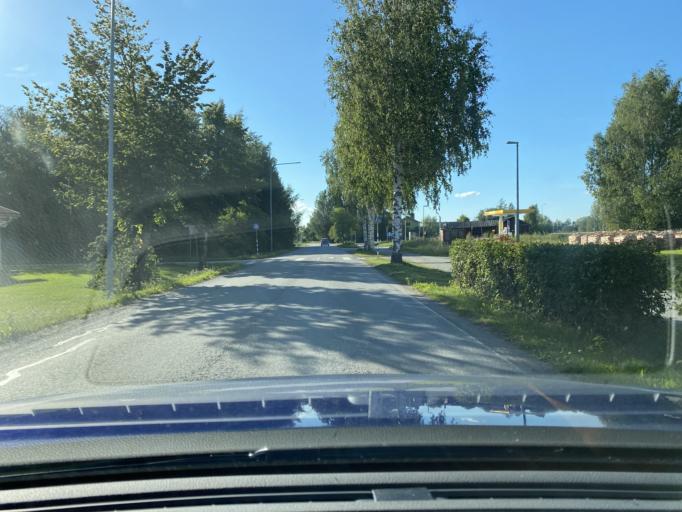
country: FI
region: Ostrobothnia
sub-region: Kyroenmaa
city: Laihia
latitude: 62.9822
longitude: 22.0022
